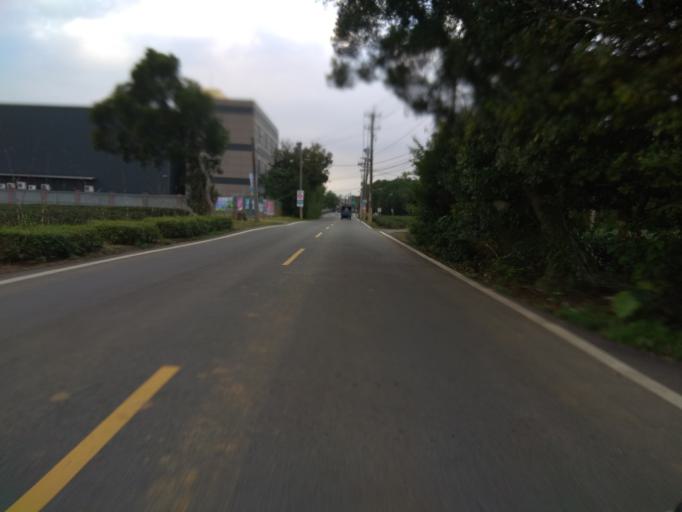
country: TW
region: Taiwan
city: Daxi
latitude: 24.8437
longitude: 121.2011
